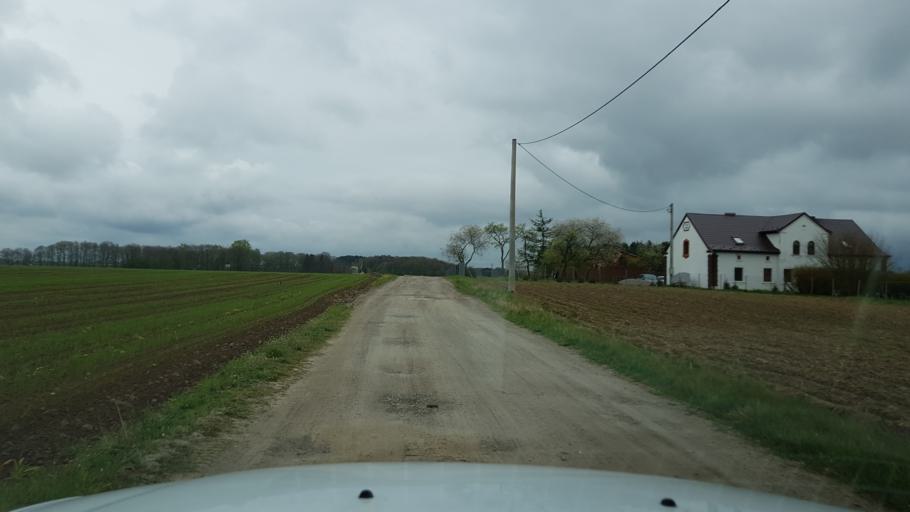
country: PL
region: West Pomeranian Voivodeship
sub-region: Powiat kolobrzeski
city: Ryman
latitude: 54.0331
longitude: 15.4797
